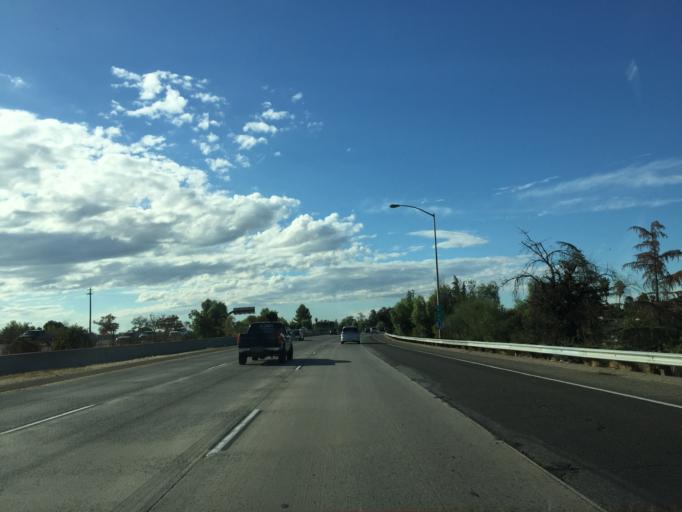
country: US
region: California
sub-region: Fresno County
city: Fresno
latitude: 36.7672
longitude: -119.7798
